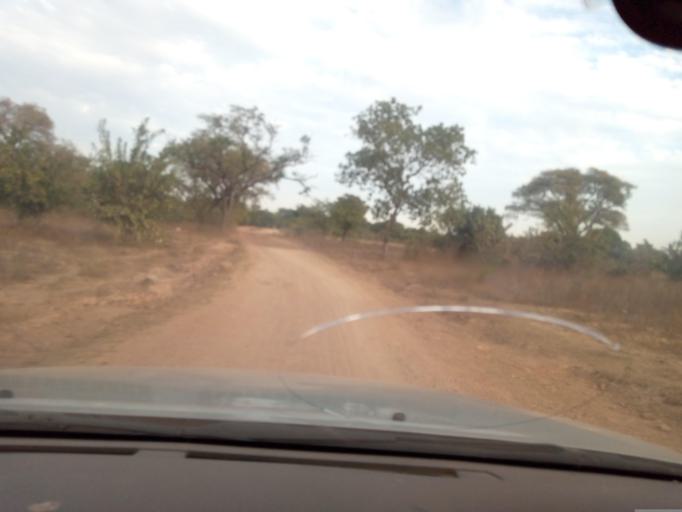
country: ML
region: Sikasso
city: Kadiolo
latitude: 10.5800
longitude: -5.8357
